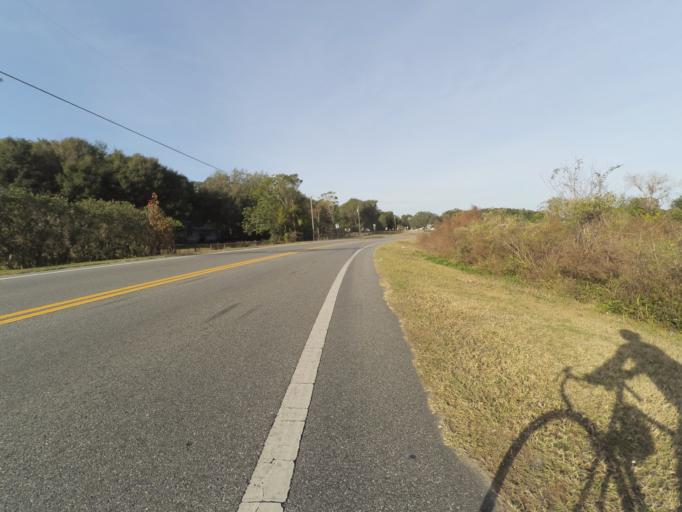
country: US
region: Florida
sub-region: Lake County
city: Umatilla
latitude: 28.9640
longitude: -81.6449
